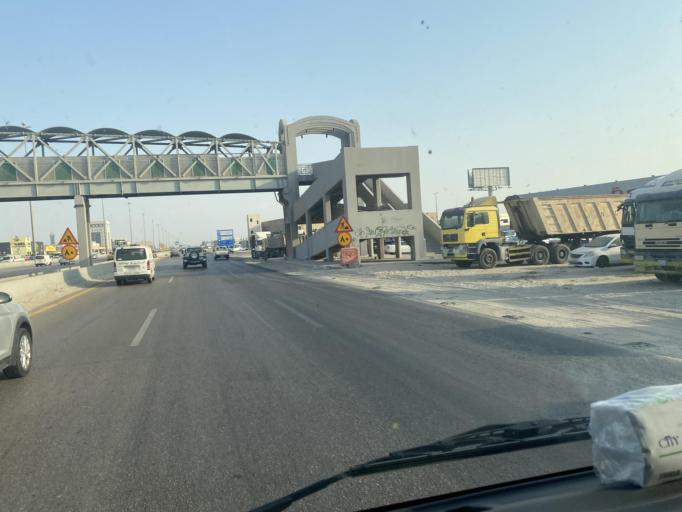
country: SA
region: Eastern Province
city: Sayhat
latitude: 26.4038
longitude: 50.0155
